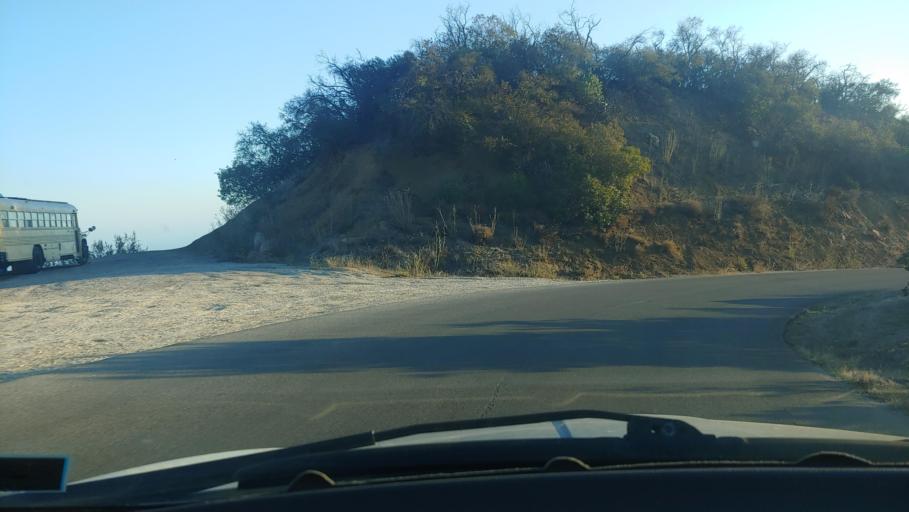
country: US
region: California
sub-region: Santa Barbara County
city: Mission Canyon
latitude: 34.4715
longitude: -119.6781
